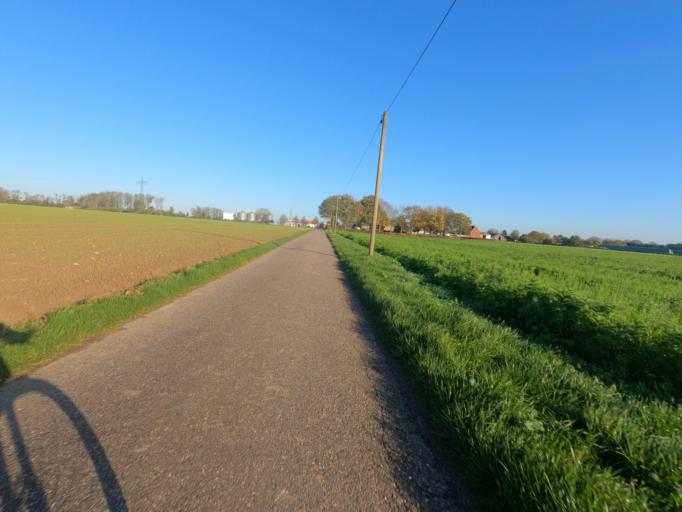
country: DE
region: North Rhine-Westphalia
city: Erkelenz
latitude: 51.0775
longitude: 6.3410
